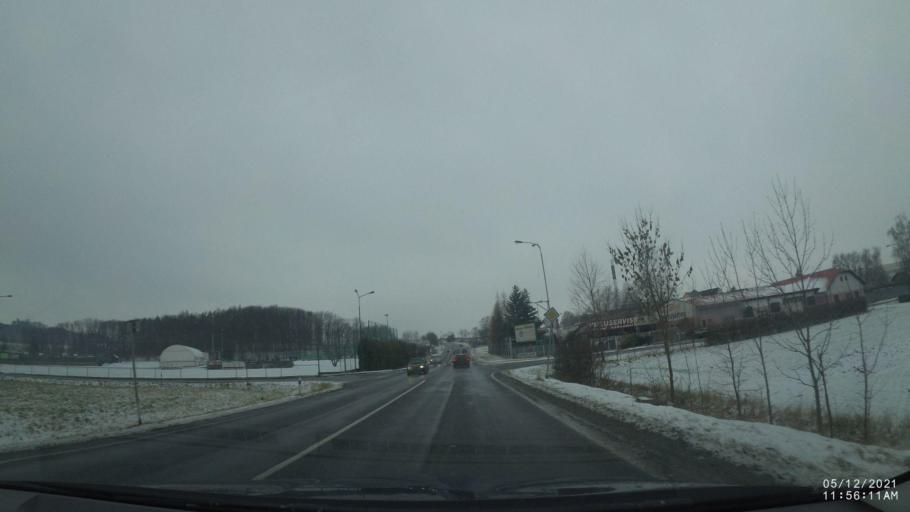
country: CZ
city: Dobruska
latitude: 50.2838
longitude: 16.1533
